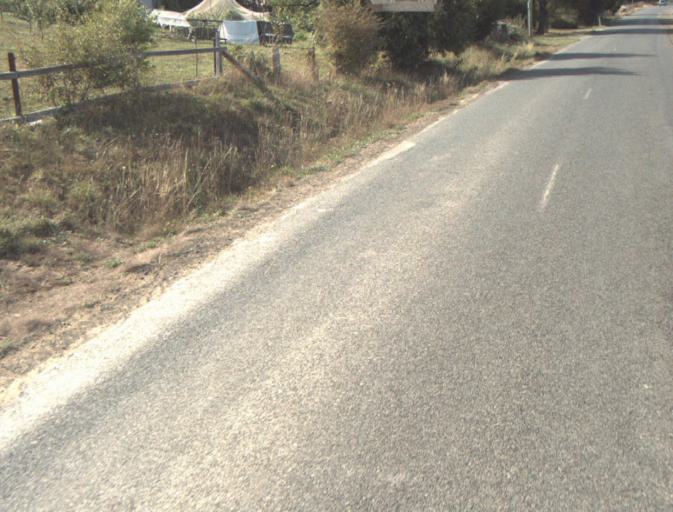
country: AU
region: Tasmania
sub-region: Launceston
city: Mayfield
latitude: -41.1819
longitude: 147.2231
